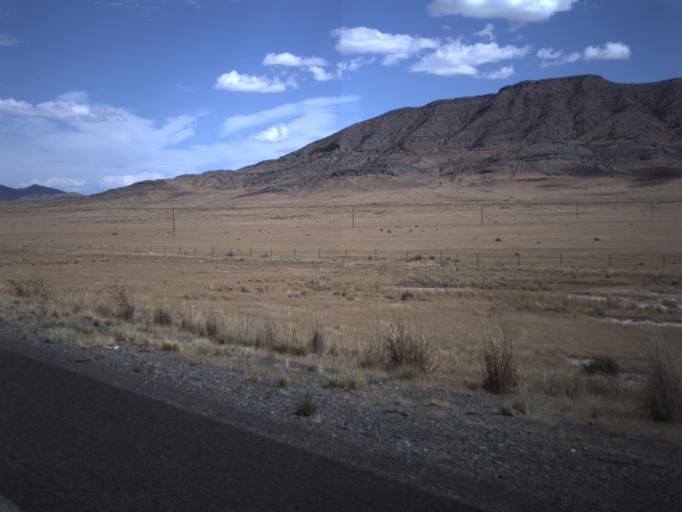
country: US
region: Utah
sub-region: Tooele County
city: Grantsville
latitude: 40.7824
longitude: -112.9654
